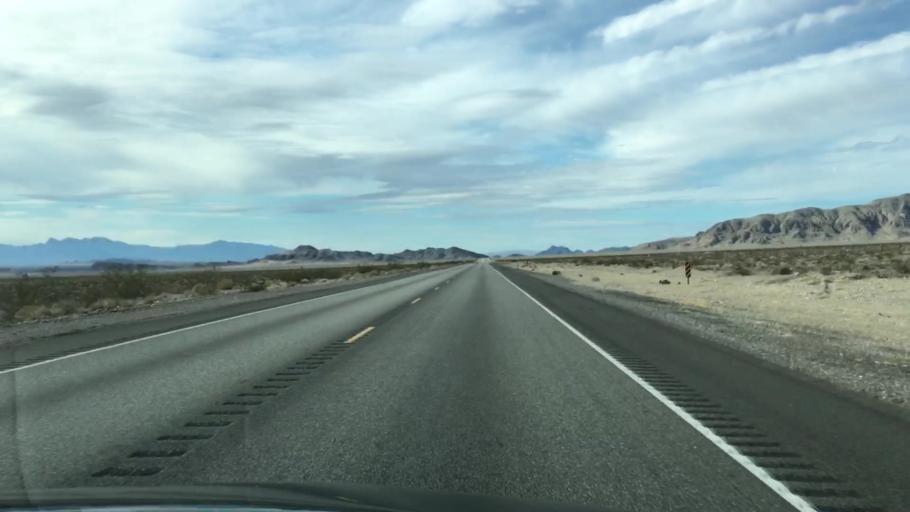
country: US
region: Nevada
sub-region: Nye County
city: Pahrump
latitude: 36.5688
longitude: -116.1503
